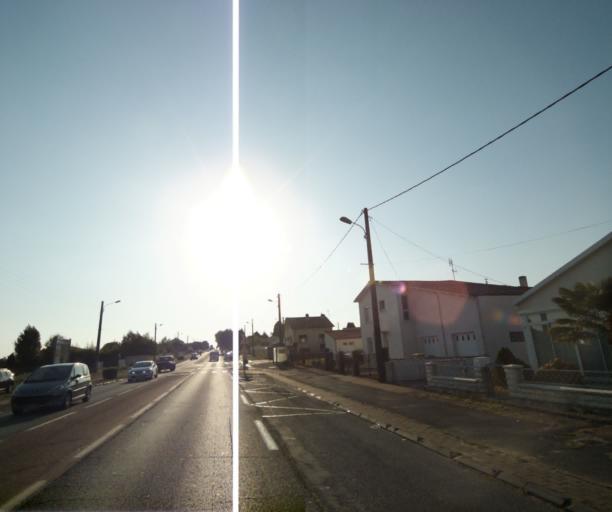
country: FR
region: Poitou-Charentes
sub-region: Departement de la Charente-Maritime
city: Tonnay-Charente
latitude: 45.9495
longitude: -0.9220
